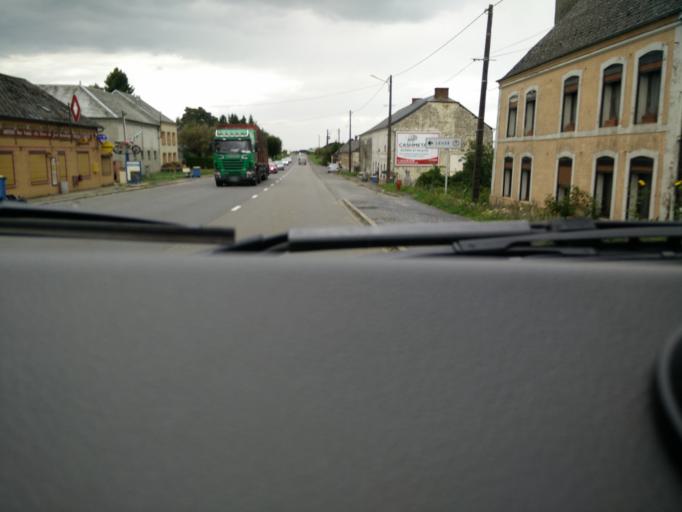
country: FR
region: Picardie
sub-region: Departement de l'Aisne
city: Saint-Michel
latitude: 49.8694
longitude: 4.1888
